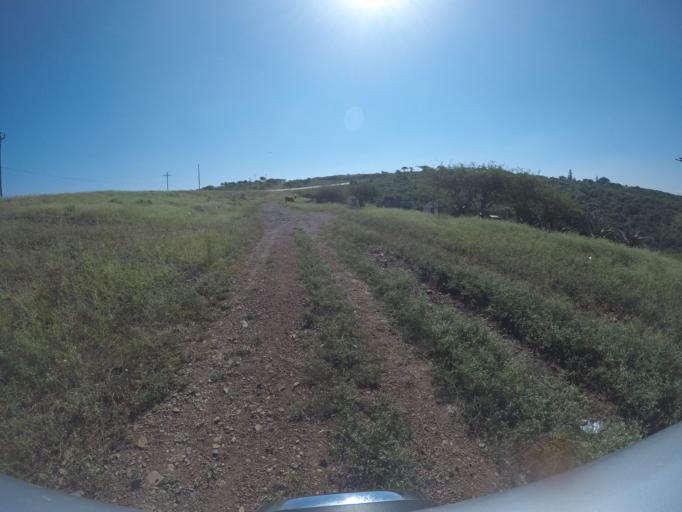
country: ZA
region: KwaZulu-Natal
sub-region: uThungulu District Municipality
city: Empangeni
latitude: -28.5708
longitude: 31.7136
